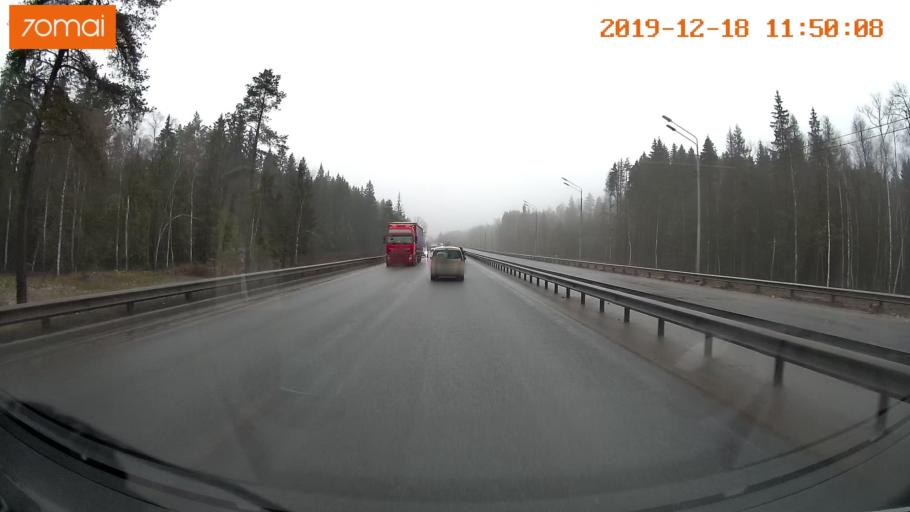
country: RU
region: Moskovskaya
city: Yershovo
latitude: 55.7834
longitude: 36.9166
